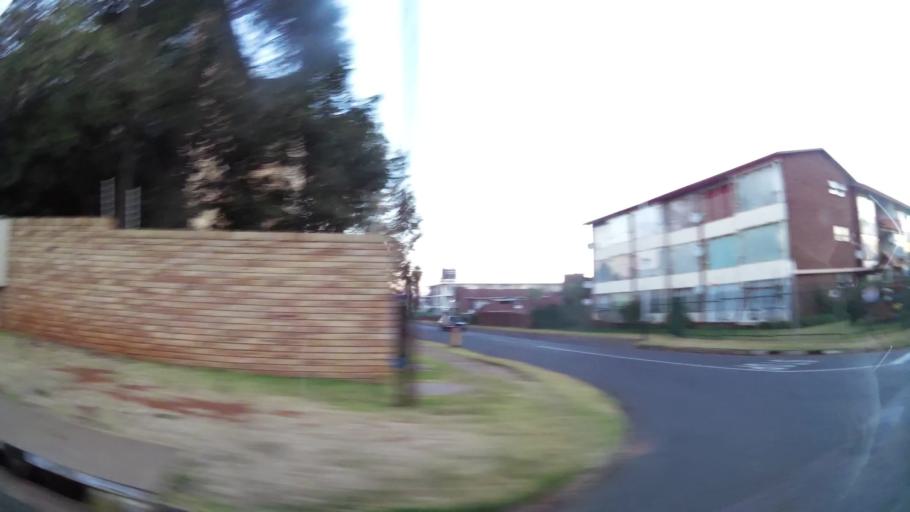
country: ZA
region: Gauteng
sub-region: City of Johannesburg Metropolitan Municipality
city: Roodepoort
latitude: -26.1691
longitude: 27.9070
